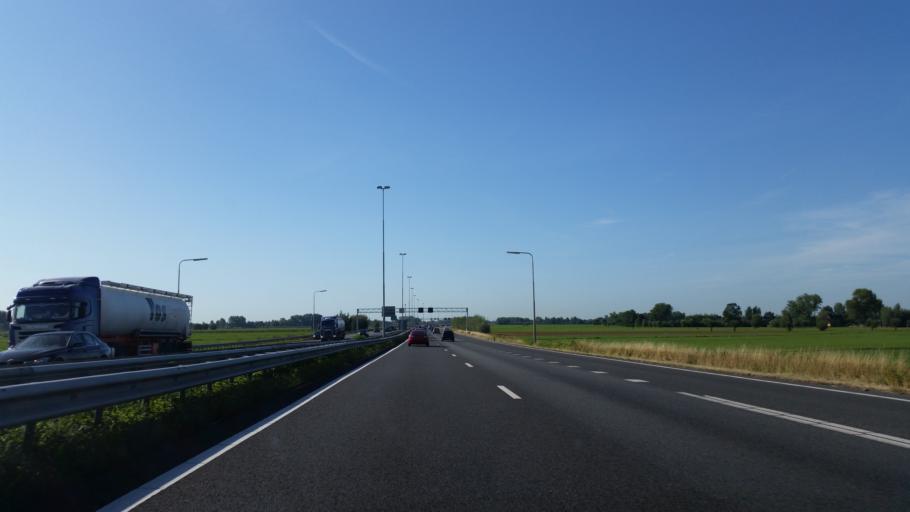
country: NL
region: South Holland
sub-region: Gemeente Gorinchem
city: Gorinchem
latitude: 51.8958
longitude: 4.9777
